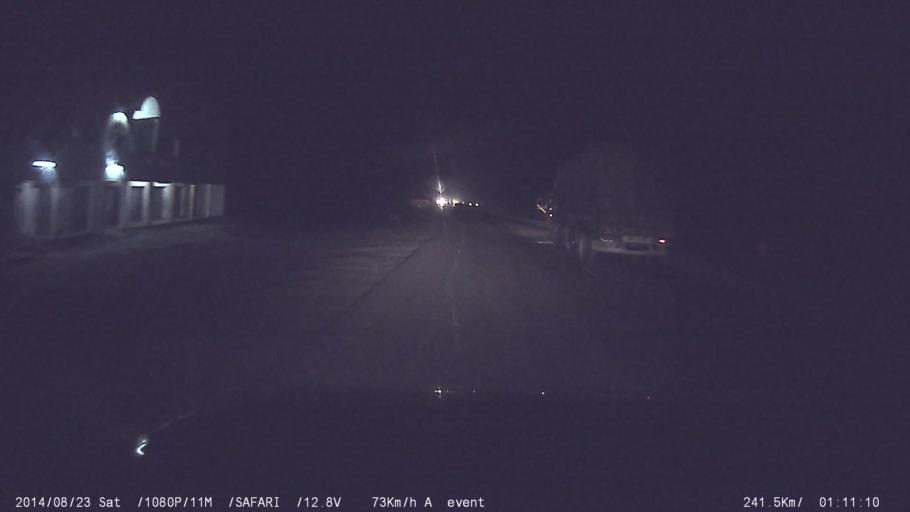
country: IN
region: Tamil Nadu
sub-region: Vellore
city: Walajapet
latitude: 12.8964
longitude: 79.5004
